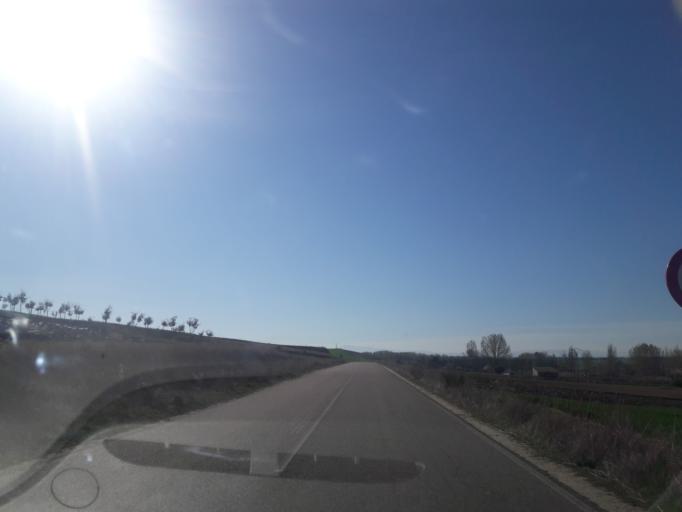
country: ES
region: Castille and Leon
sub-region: Provincia de Salamanca
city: Tordillos
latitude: 40.8565
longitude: -5.3482
